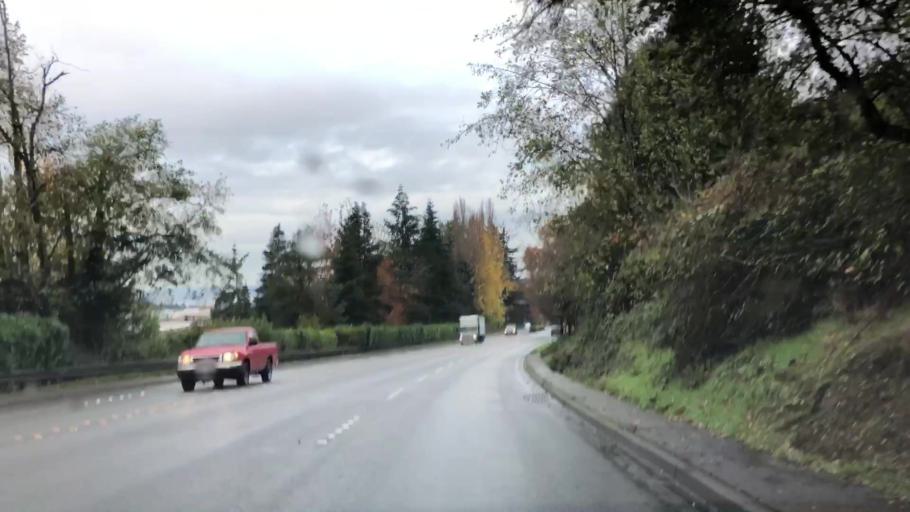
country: US
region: Washington
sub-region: King County
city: Mercer Island
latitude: 47.5799
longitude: -122.2305
